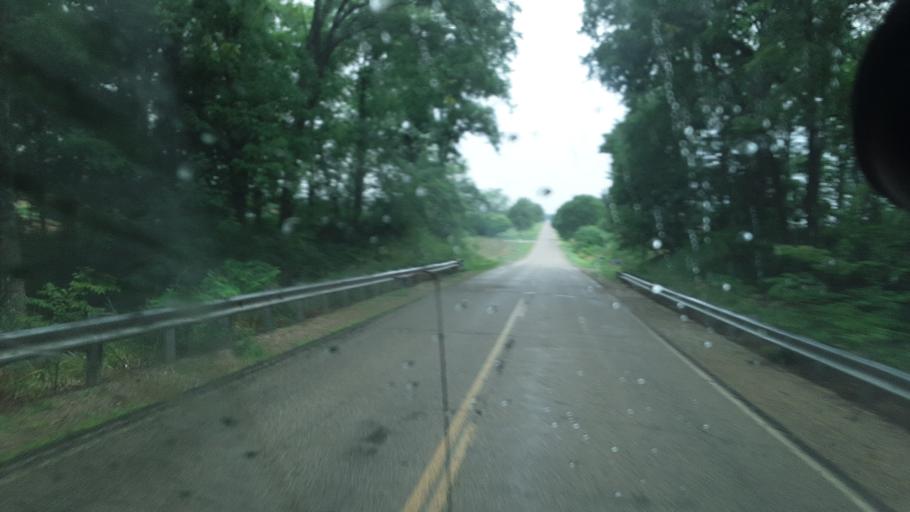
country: US
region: Michigan
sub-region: Hillsdale County
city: Reading
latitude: 41.7081
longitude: -84.7271
